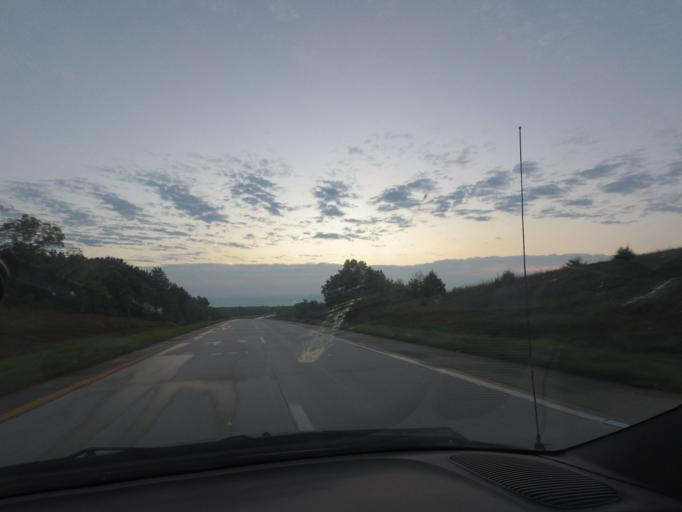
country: US
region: Missouri
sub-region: Macon County
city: Macon
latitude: 39.7568
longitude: -92.6057
